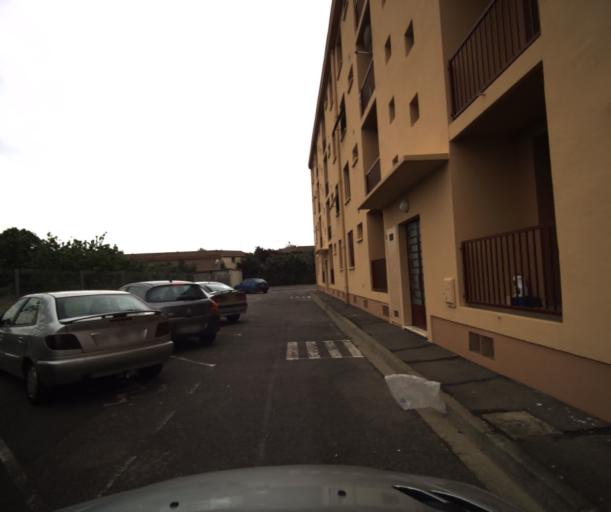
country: FR
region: Midi-Pyrenees
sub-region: Departement de la Haute-Garonne
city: Portet-sur-Garonne
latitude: 43.5231
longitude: 1.4006
